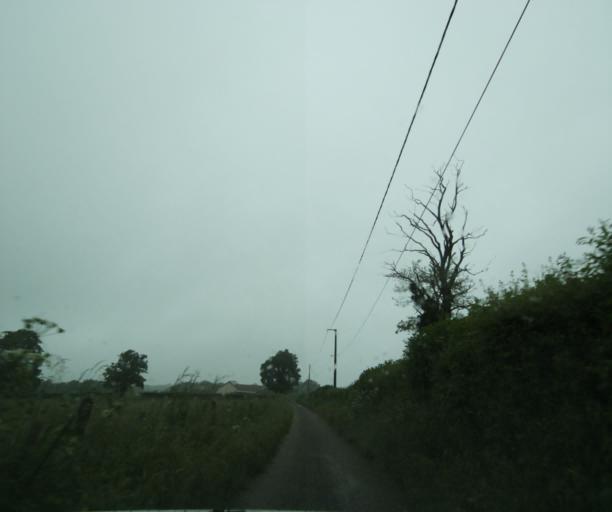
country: FR
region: Bourgogne
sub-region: Departement de Saone-et-Loire
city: La Clayette
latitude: 46.3680
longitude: 4.3526
